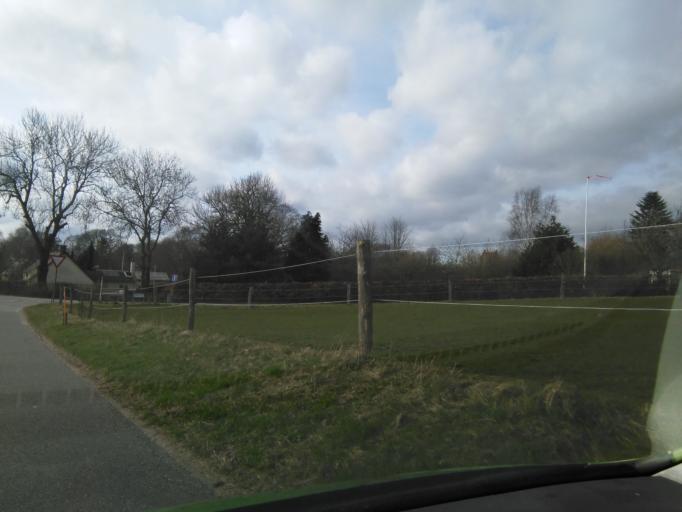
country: DK
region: Central Jutland
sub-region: Arhus Kommune
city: Trige
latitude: 56.2072
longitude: 10.1321
